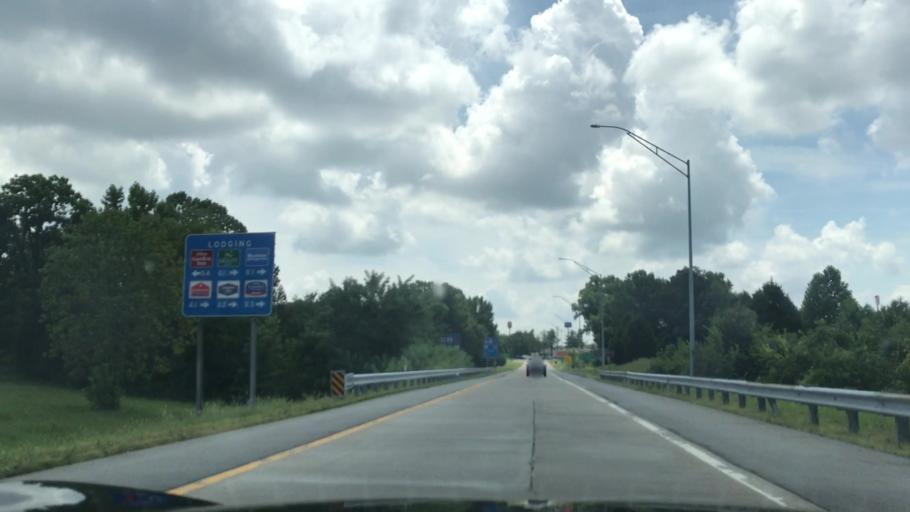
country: US
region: Tennessee
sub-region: Montgomery County
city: Clarksville
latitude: 36.6020
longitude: -87.2855
